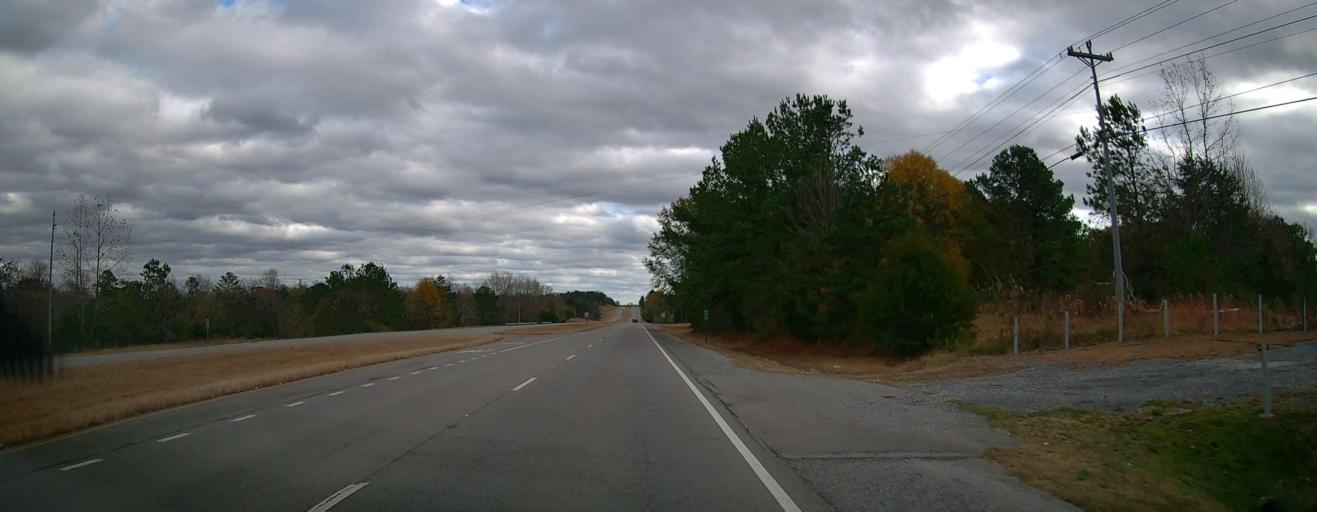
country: US
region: Alabama
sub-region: Lawrence County
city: Town Creek
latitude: 34.5861
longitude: -87.4196
